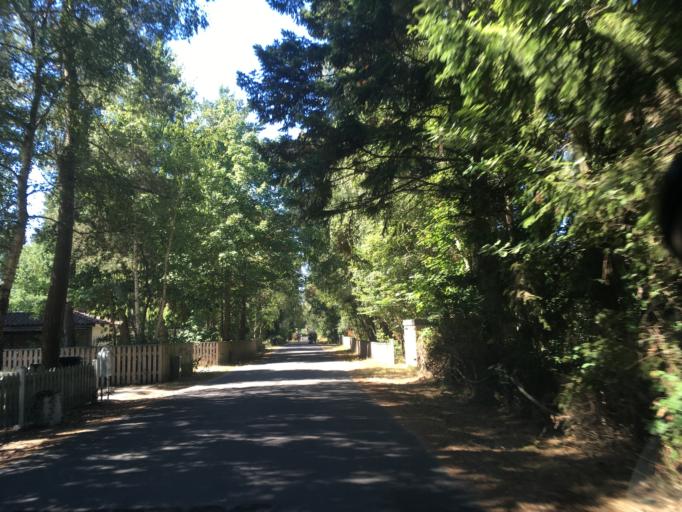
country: SE
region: Skane
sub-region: Vellinge Kommun
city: Hollviken
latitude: 55.4125
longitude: 12.9662
